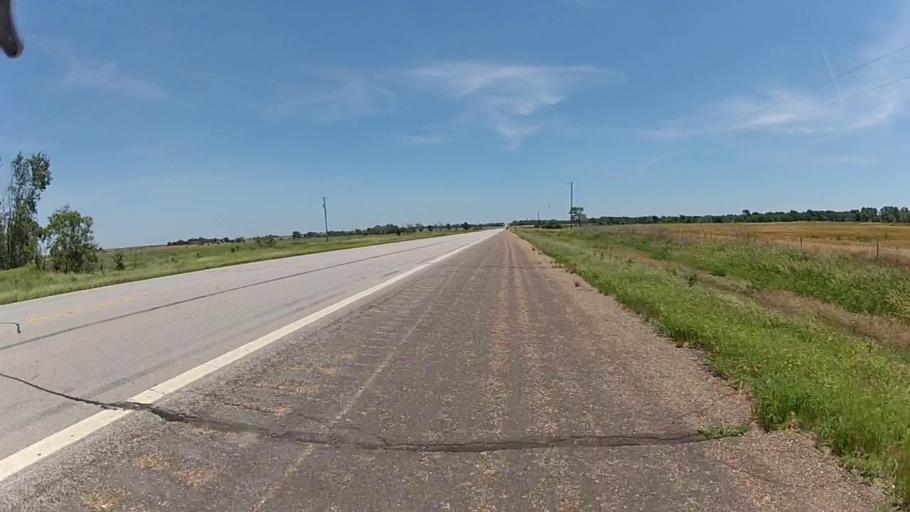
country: US
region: Kansas
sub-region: Barber County
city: Medicine Lodge
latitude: 37.2538
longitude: -98.3218
